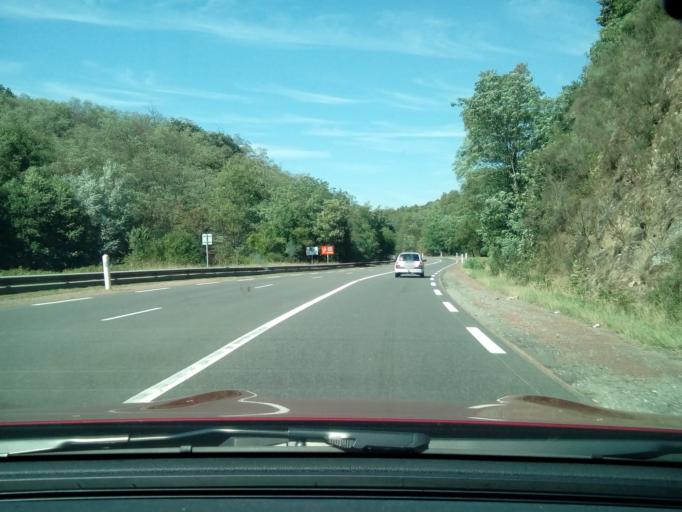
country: FR
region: Rhone-Alpes
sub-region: Departement du Rhone
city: Lissieu
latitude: 45.8477
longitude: 4.7188
